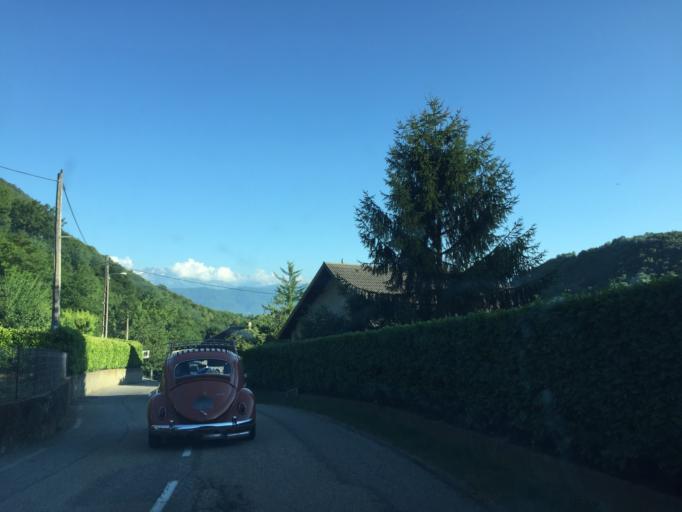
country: FR
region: Rhone-Alpes
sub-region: Departement de la Savoie
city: Challes-les-Eaux
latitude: 45.5426
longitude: 6.0063
